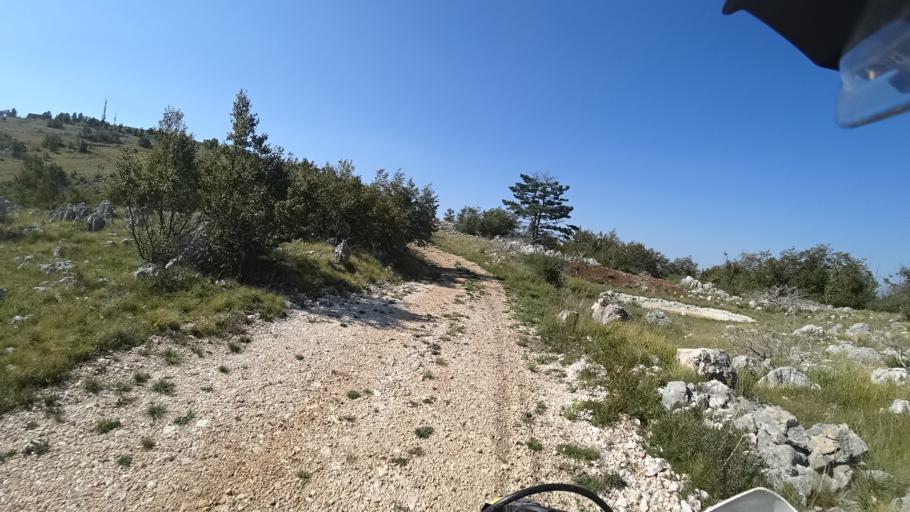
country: HR
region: Sibensko-Kniniska
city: Drnis
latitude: 43.9288
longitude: 16.1678
